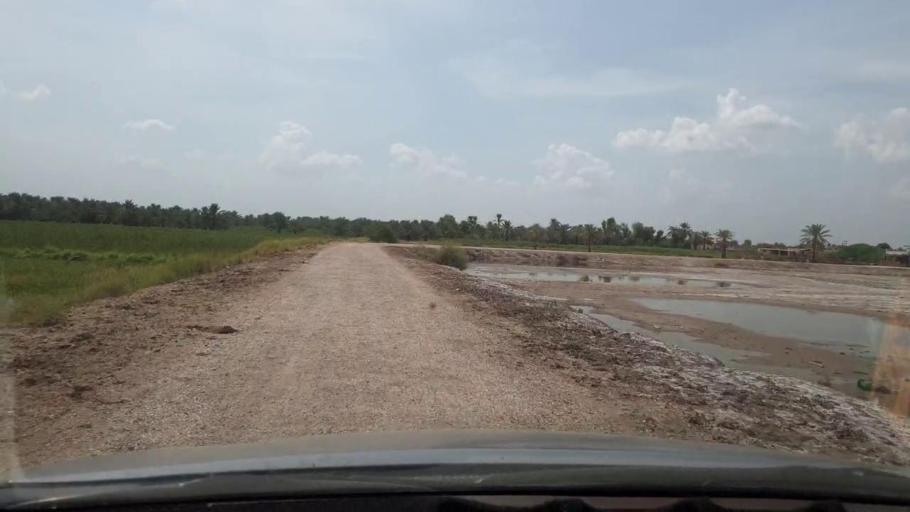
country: PK
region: Sindh
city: Khairpur
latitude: 27.4563
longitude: 68.8248
